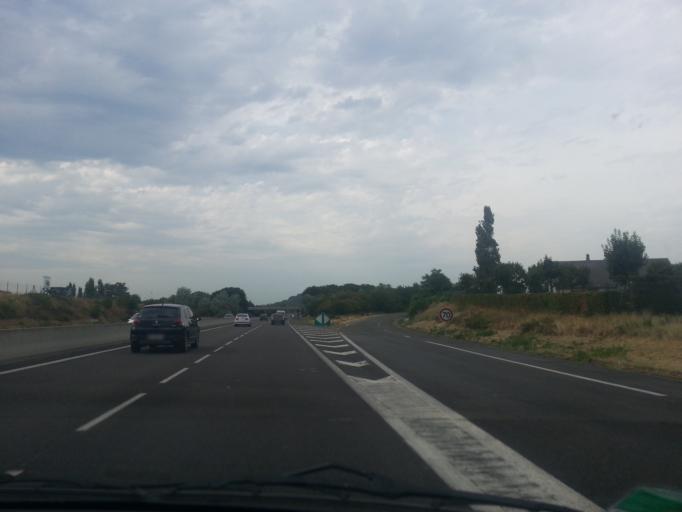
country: FR
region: Auvergne
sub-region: Departement du Puy-de-Dome
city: Perignat-les-Sarlieve
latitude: 45.7566
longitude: 3.1410
